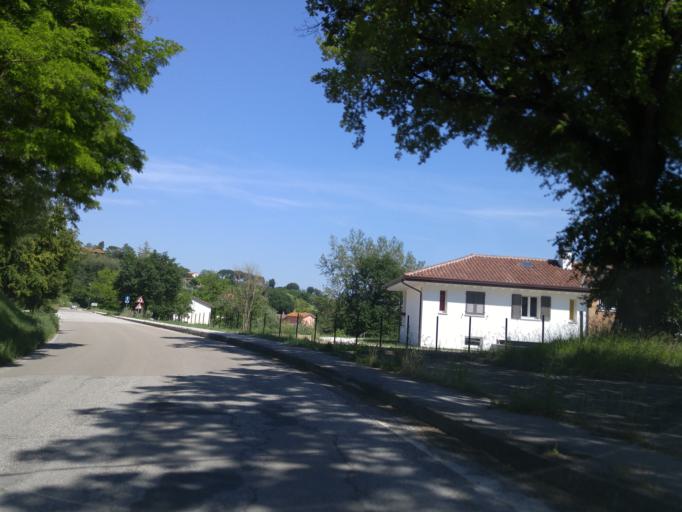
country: IT
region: The Marches
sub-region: Provincia di Pesaro e Urbino
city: Montefelcino
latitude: 43.7255
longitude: 12.8294
